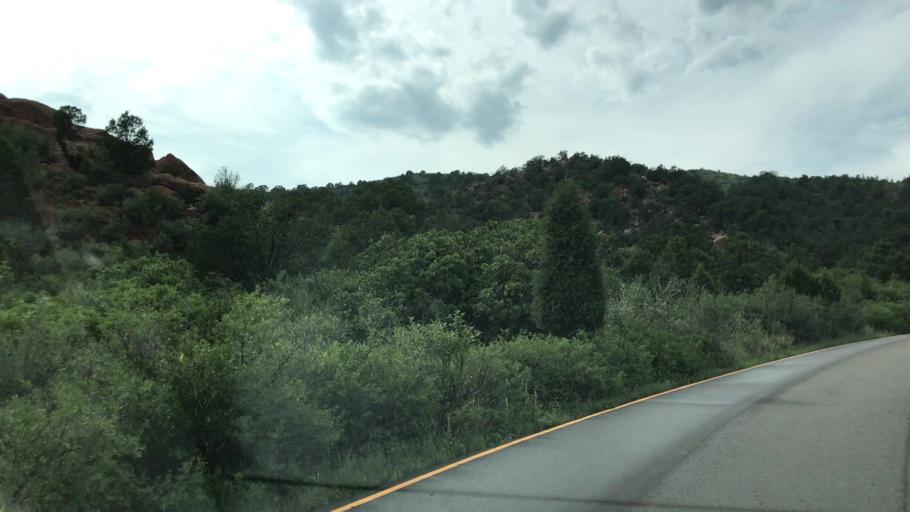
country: US
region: Colorado
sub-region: El Paso County
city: Manitou Springs
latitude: 38.8817
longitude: -104.8817
